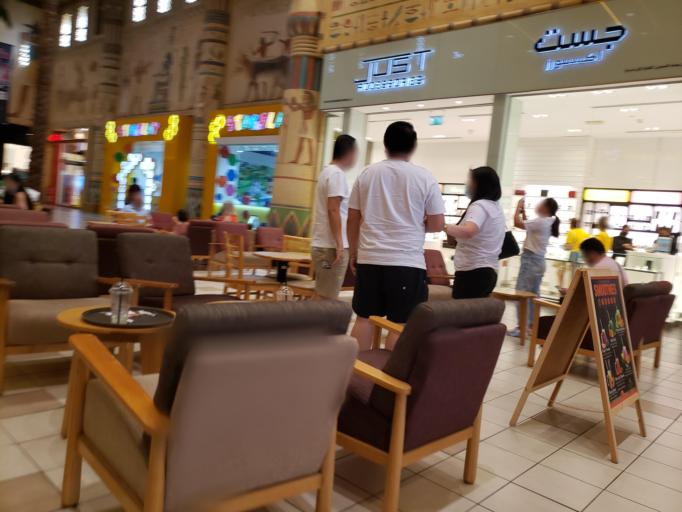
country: AE
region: Dubai
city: Dubai
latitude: 25.0440
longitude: 55.1183
